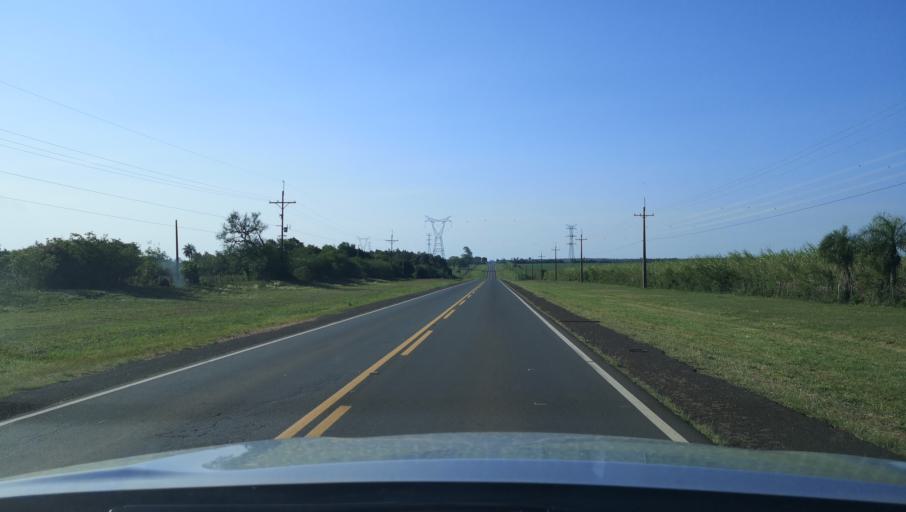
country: PY
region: Misiones
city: Santa Maria
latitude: -26.7939
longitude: -57.0237
